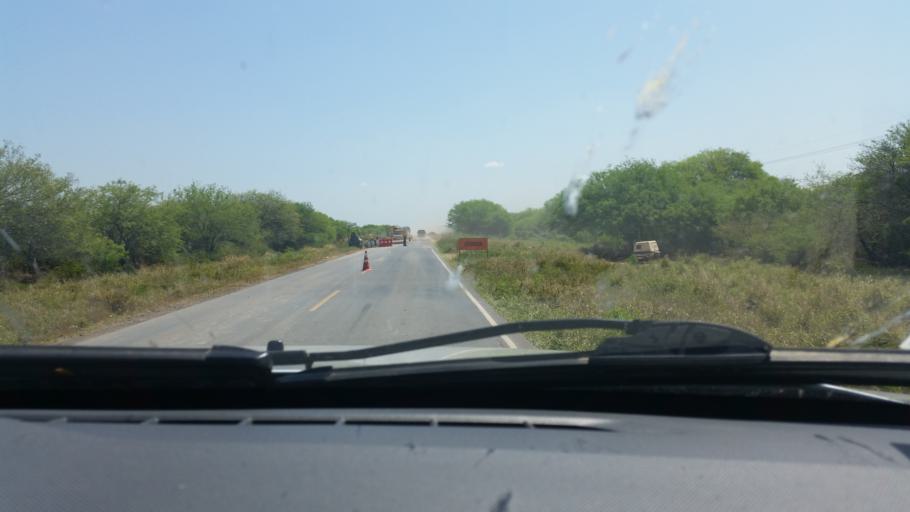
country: PY
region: Boqueron
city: Colonia Menno
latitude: -22.7364
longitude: -59.6777
